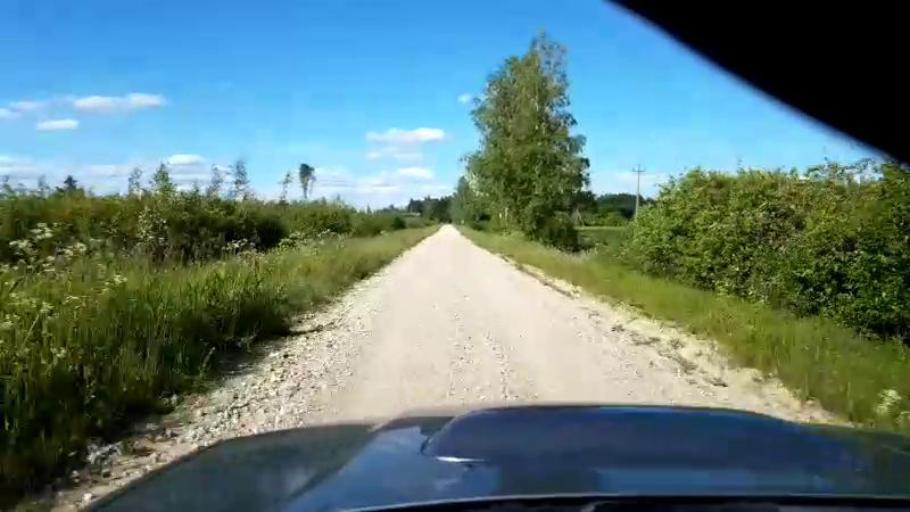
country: EE
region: Paernumaa
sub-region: Sauga vald
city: Sauga
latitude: 58.5016
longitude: 24.5642
